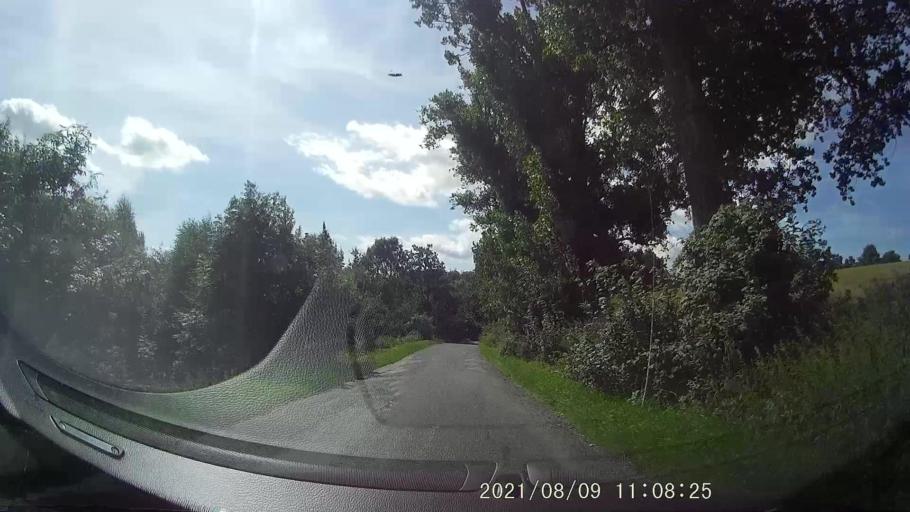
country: PL
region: Lower Silesian Voivodeship
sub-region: Powiat klodzki
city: Klodzko
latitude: 50.4553
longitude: 16.6089
